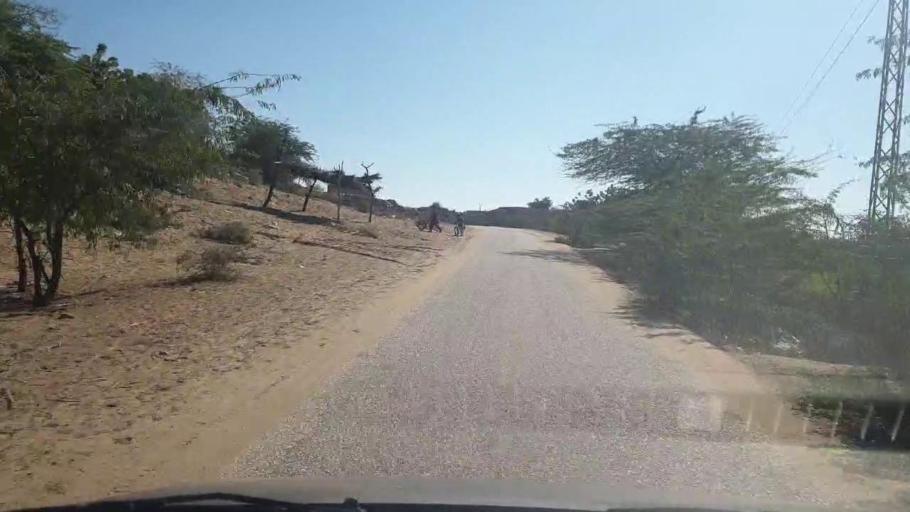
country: PK
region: Sindh
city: Bozdar
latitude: 27.0572
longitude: 68.6450
